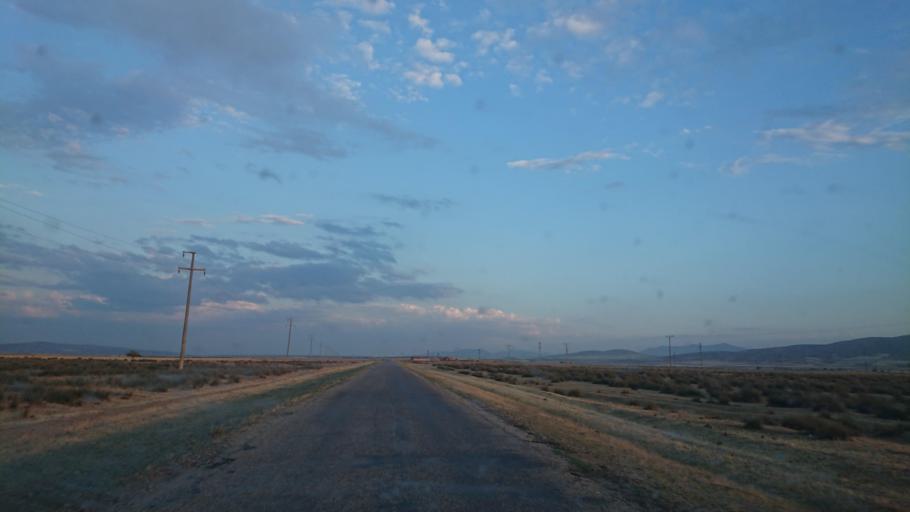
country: TR
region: Aksaray
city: Agacoren
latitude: 38.8803
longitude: 34.0563
